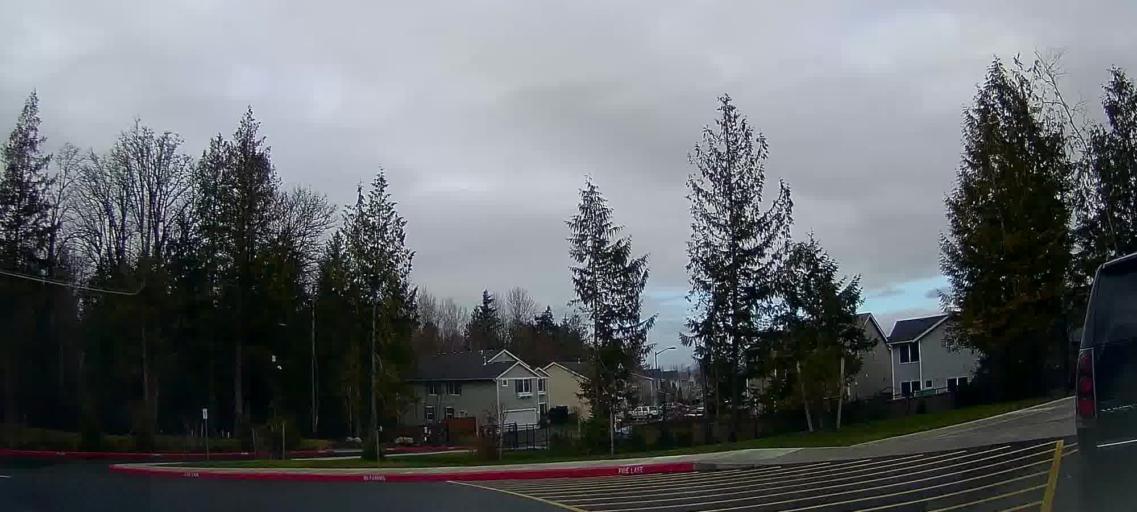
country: US
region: Washington
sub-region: Skagit County
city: Big Lake
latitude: 48.4241
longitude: -122.2740
